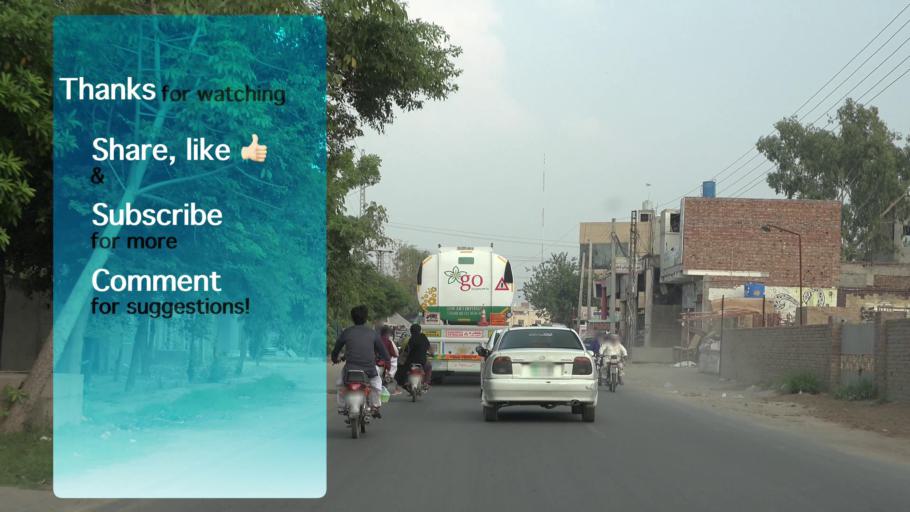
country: PK
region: Punjab
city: Faisalabad
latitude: 31.4421
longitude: 73.1334
